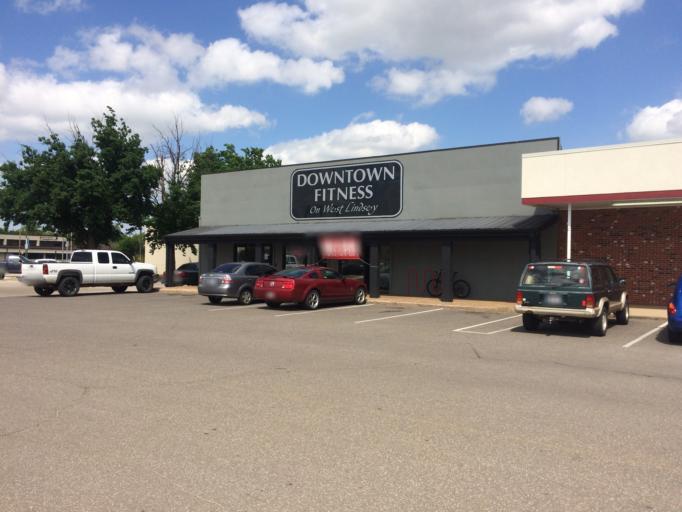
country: US
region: Oklahoma
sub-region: Cleveland County
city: Norman
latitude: 35.2030
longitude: -97.4655
